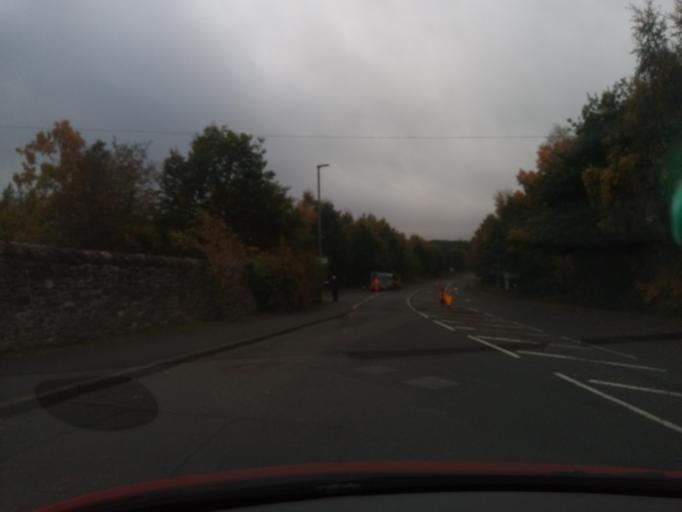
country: GB
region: Scotland
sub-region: The Scottish Borders
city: Galashiels
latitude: 55.6176
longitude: -2.8768
